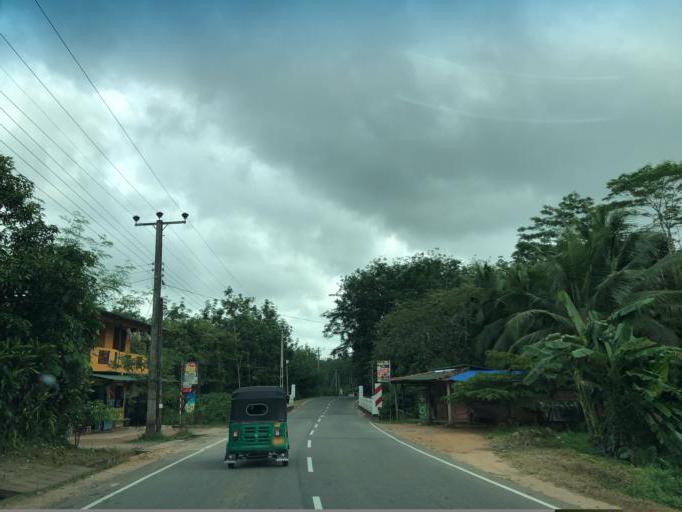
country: LK
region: Western
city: Horana South
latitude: 6.6856
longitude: 80.1015
